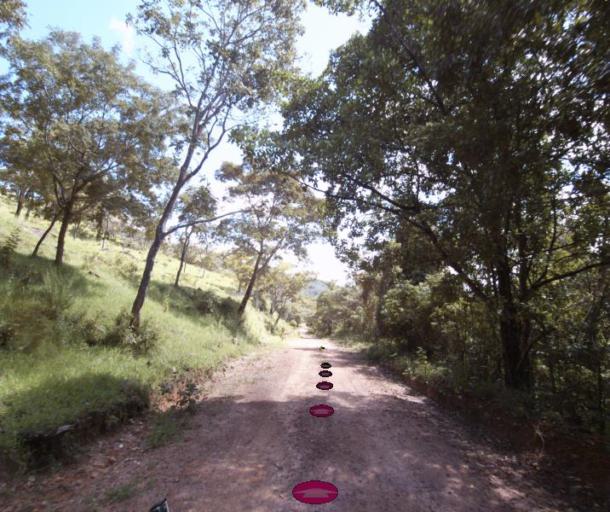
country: BR
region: Goias
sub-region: Pirenopolis
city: Pirenopolis
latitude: -15.7831
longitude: -48.9446
